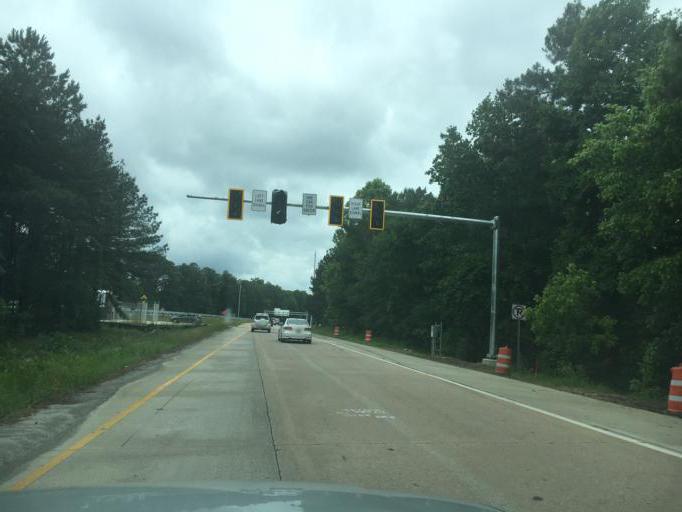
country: US
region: Georgia
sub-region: Gwinnett County
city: Dacula
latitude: 34.0755
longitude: -83.9195
